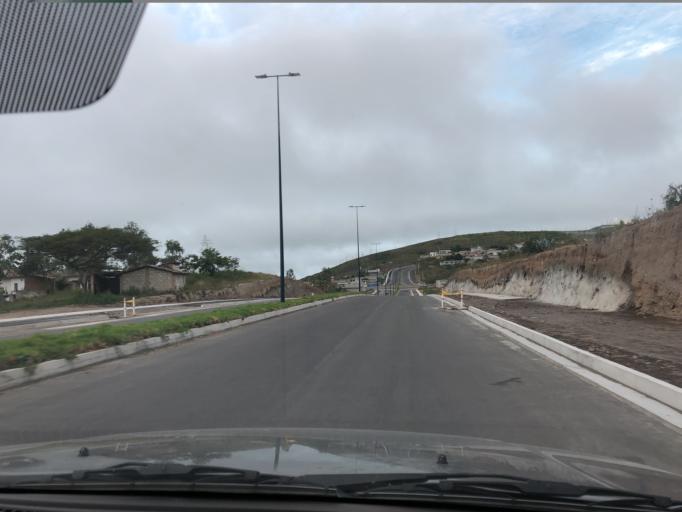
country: EC
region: Imbabura
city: Ibarra
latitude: 0.3612
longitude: -78.1395
